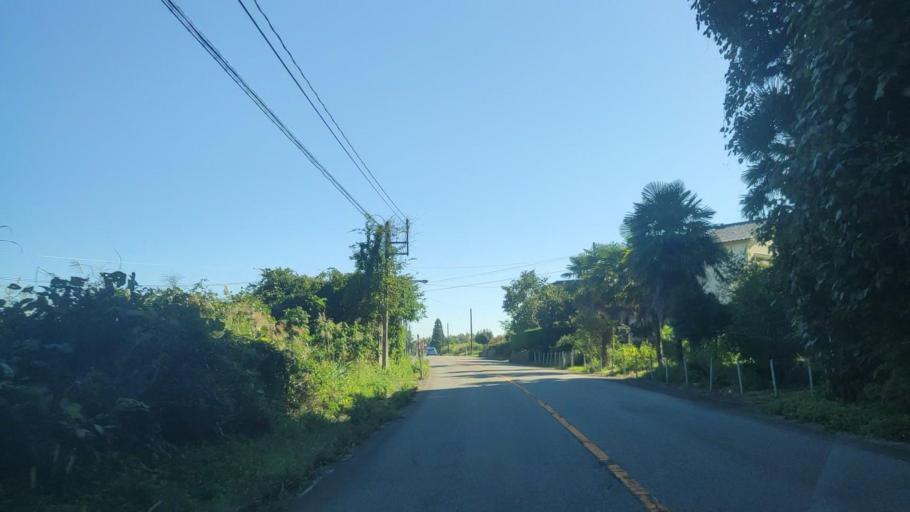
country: JP
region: Ishikawa
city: Nanao
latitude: 37.2607
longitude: 137.0889
